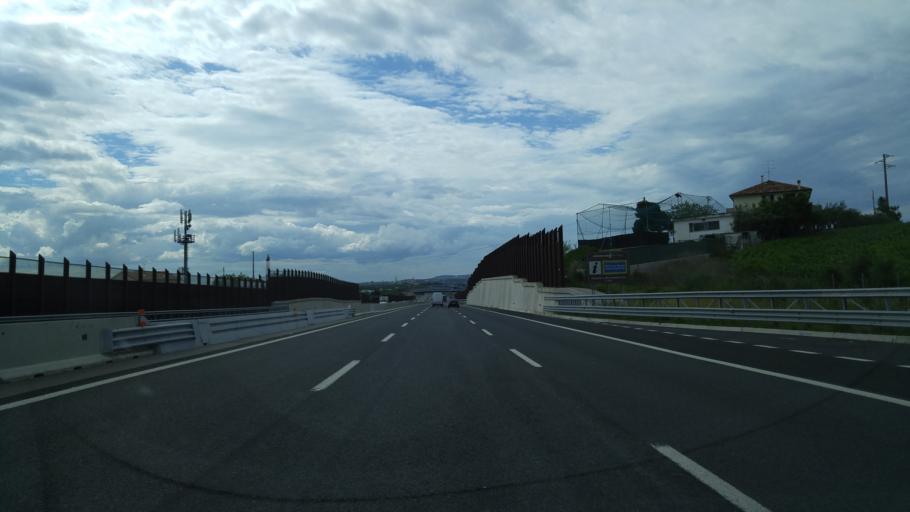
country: IT
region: Emilia-Romagna
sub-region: Provincia di Rimini
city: Riccione
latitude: 43.9816
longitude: 12.6506
